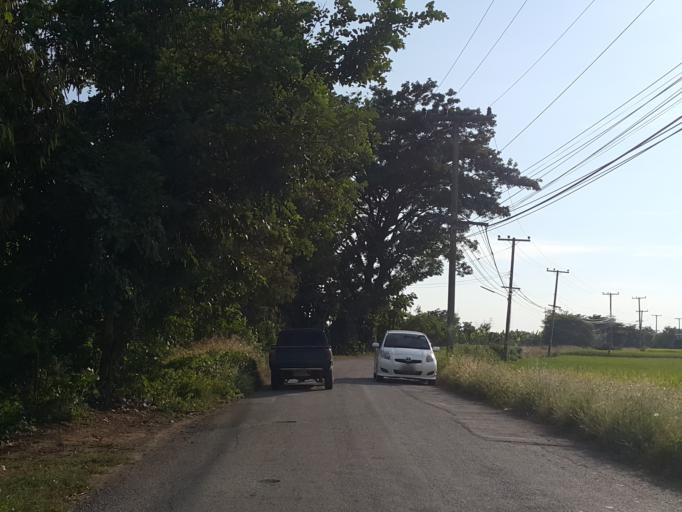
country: TH
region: Chiang Mai
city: San Kamphaeng
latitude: 18.8199
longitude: 99.1679
